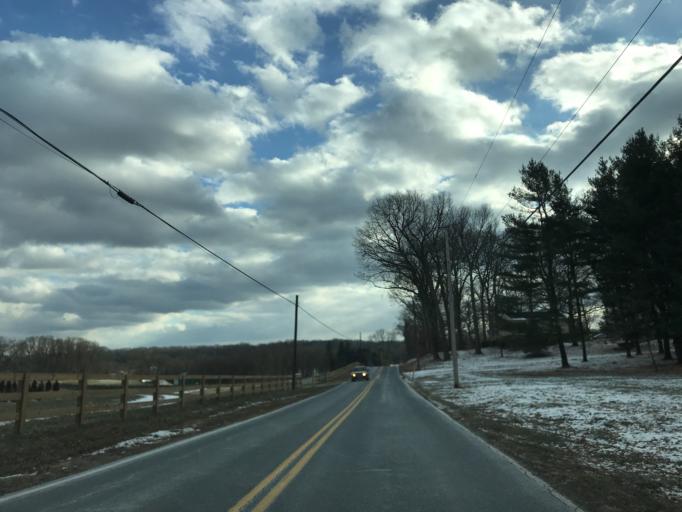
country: US
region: Pennsylvania
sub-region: York County
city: Susquehanna Trails
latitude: 39.6611
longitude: -76.3832
